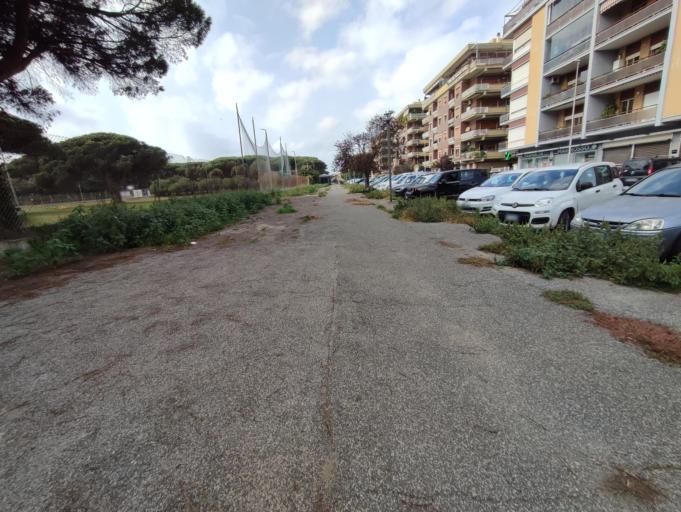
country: IT
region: Latium
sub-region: Citta metropolitana di Roma Capitale
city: Lido di Ostia
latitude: 41.7324
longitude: 12.3015
